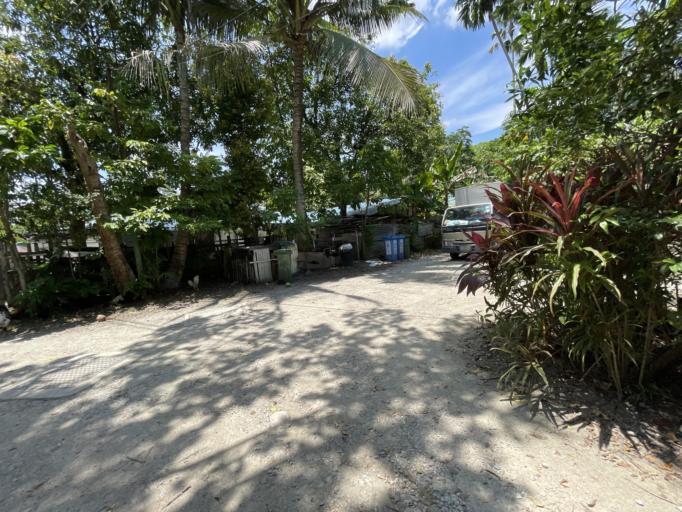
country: MY
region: Johor
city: Kampung Pasir Gudang Baru
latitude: 1.3842
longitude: 103.8789
